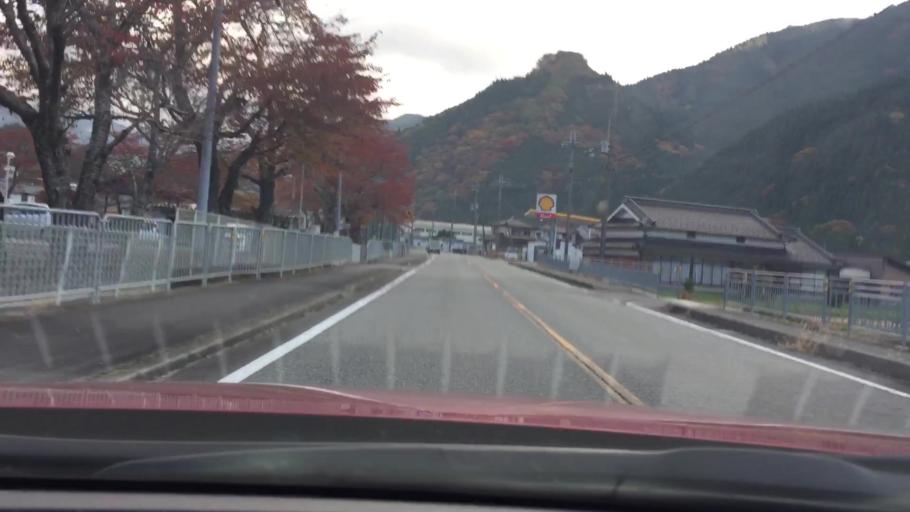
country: JP
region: Hyogo
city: Yamazakicho-nakabirose
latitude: 35.1528
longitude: 134.5433
